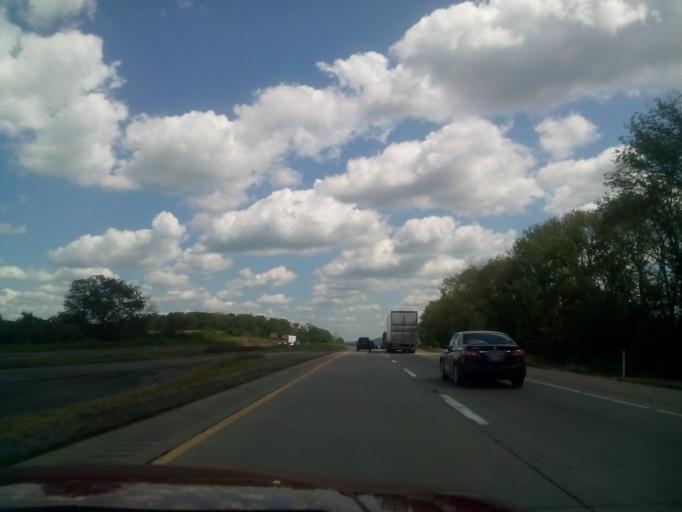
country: US
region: Pennsylvania
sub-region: Northumberland County
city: Riverside
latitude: 40.9871
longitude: -76.7031
